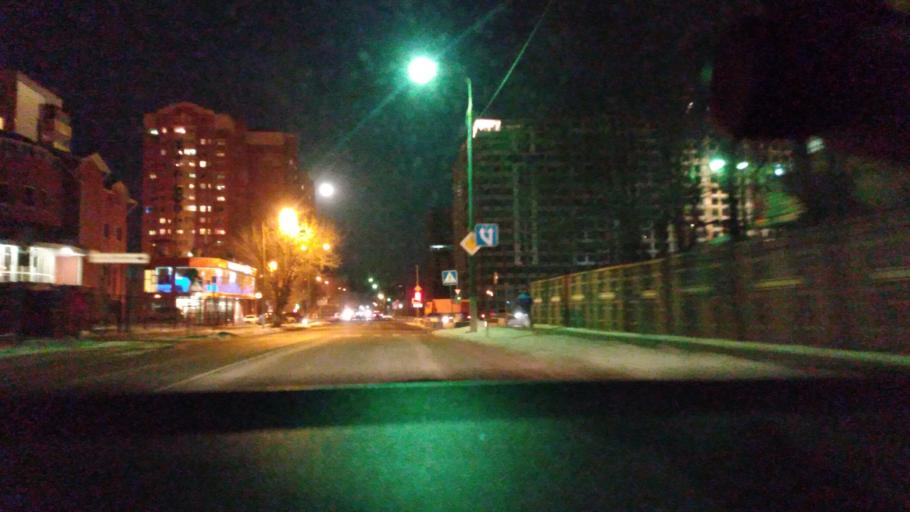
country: RU
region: Moskovskaya
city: Zheleznodorozhnyy
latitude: 55.7434
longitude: 38.0331
